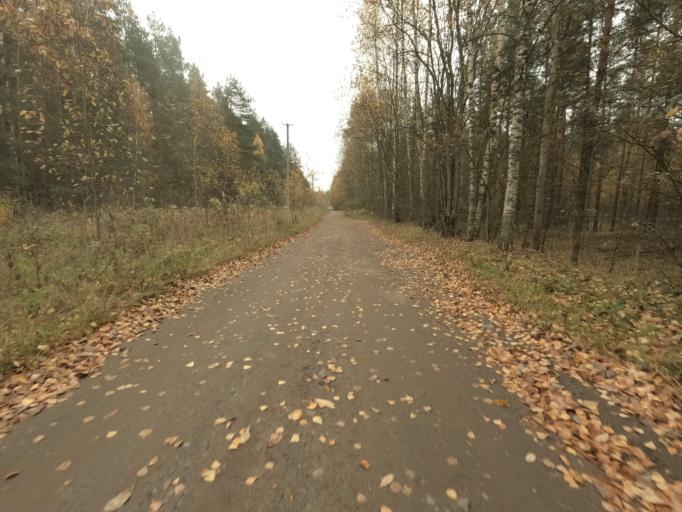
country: RU
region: Leningrad
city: Kirovsk
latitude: 59.8561
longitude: 30.9892
